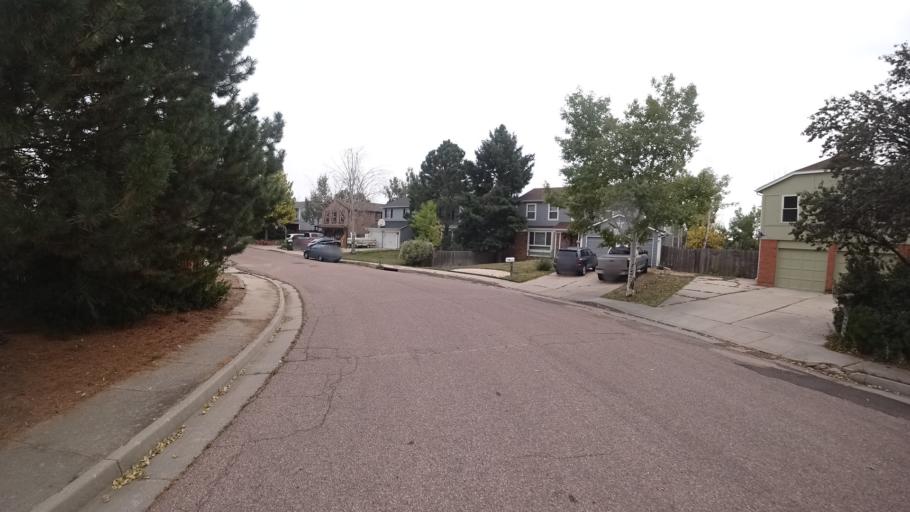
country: US
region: Colorado
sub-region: El Paso County
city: Cimarron Hills
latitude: 38.9021
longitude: -104.7379
